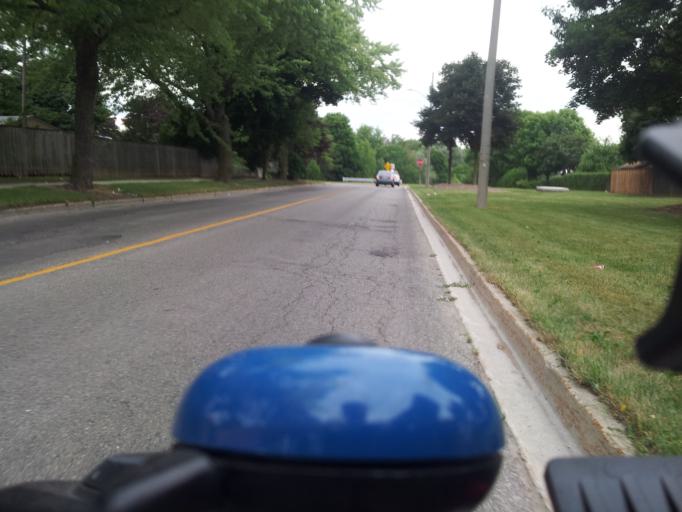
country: CA
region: Ontario
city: Stratford
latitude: 43.3741
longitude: -80.9481
